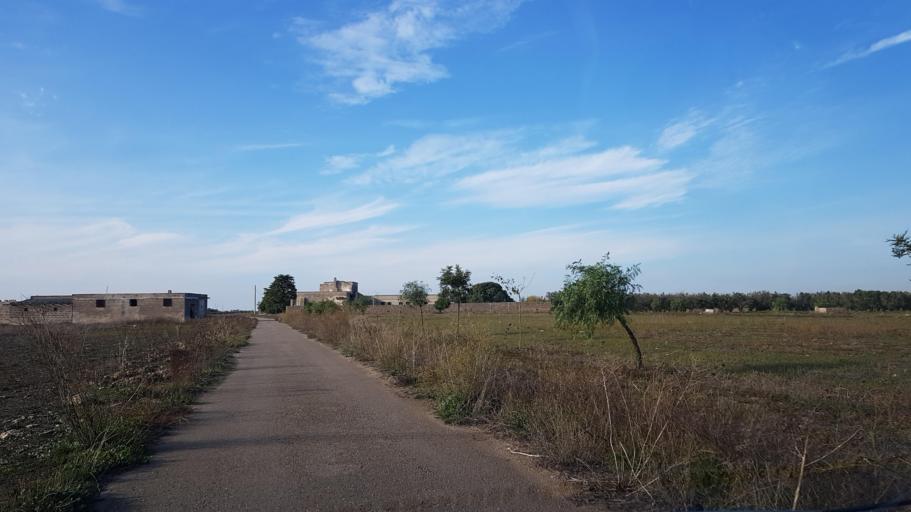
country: IT
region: Apulia
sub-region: Provincia di Brindisi
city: Mesagne
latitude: 40.4952
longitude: 17.8530
